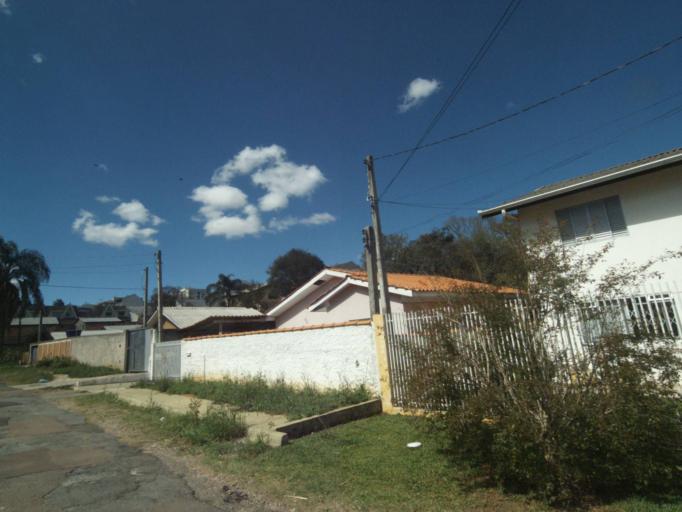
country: BR
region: Parana
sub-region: Curitiba
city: Curitiba
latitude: -25.3820
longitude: -49.2411
